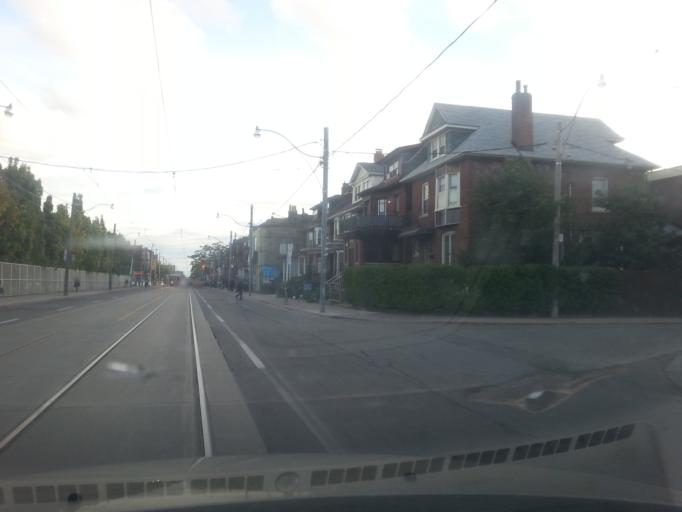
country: CA
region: Ontario
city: Toronto
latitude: 43.6628
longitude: -79.4103
